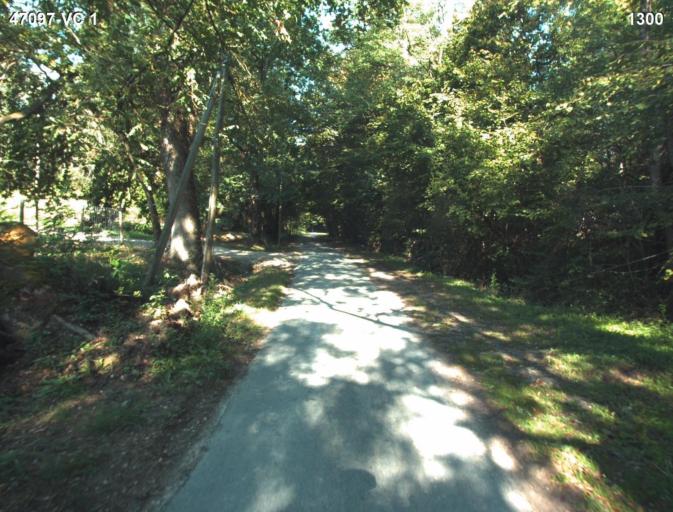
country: FR
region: Aquitaine
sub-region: Departement du Lot-et-Garonne
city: Vianne
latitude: 44.2127
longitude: 0.3556
